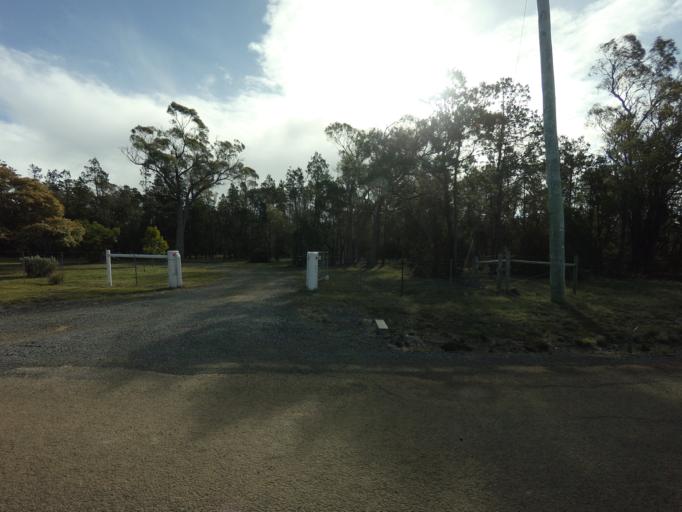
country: AU
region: Tasmania
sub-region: Sorell
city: Sorell
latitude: -42.3048
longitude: 147.9913
